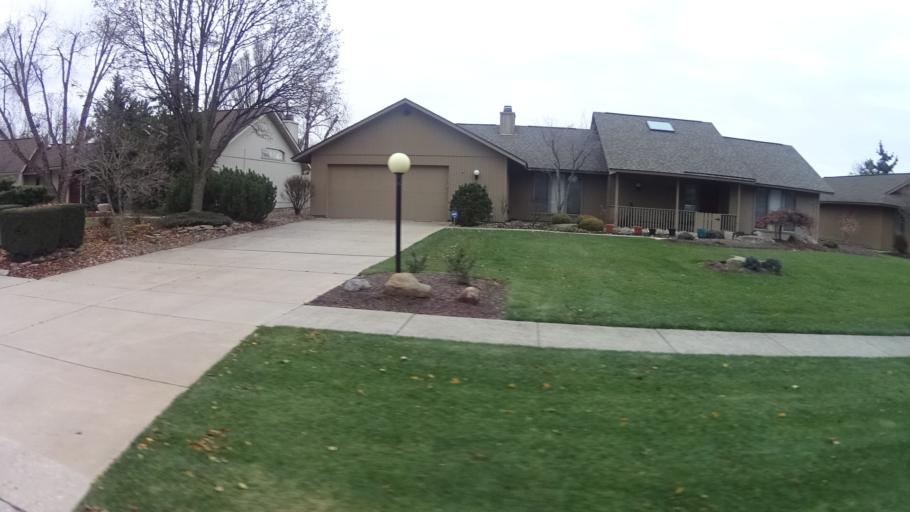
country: US
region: Ohio
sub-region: Lorain County
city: North Ridgeville
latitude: 41.3686
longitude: -81.9847
